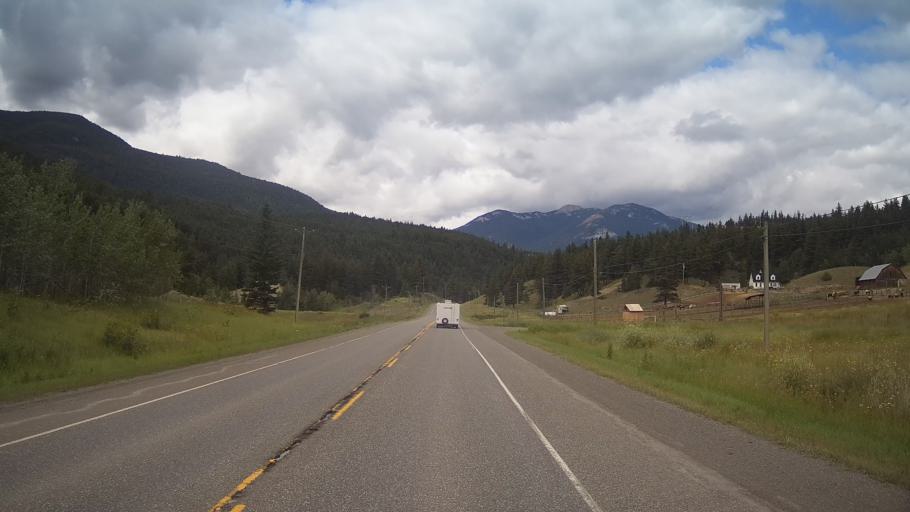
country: CA
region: British Columbia
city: Cache Creek
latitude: 51.0624
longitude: -121.5661
